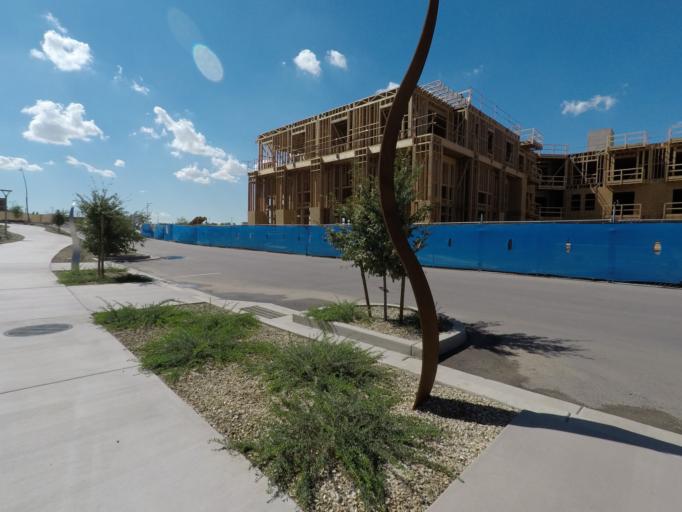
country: US
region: Arizona
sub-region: Maricopa County
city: Tempe
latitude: 33.4340
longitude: -111.8987
